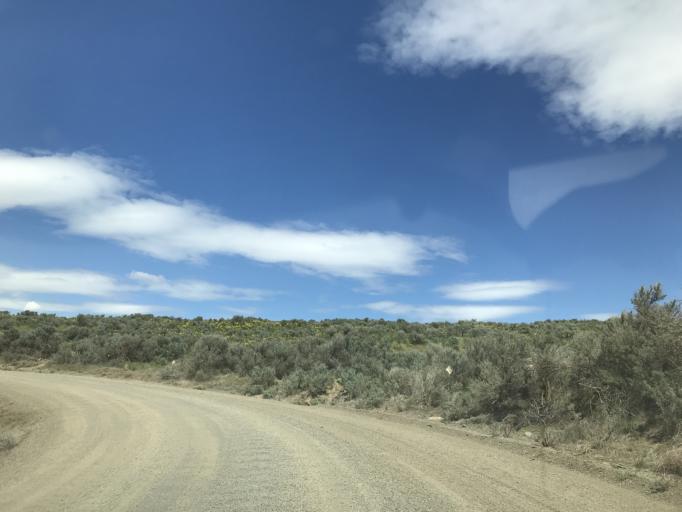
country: US
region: Washington
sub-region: Grant County
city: Quincy
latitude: 47.3131
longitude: -119.8198
